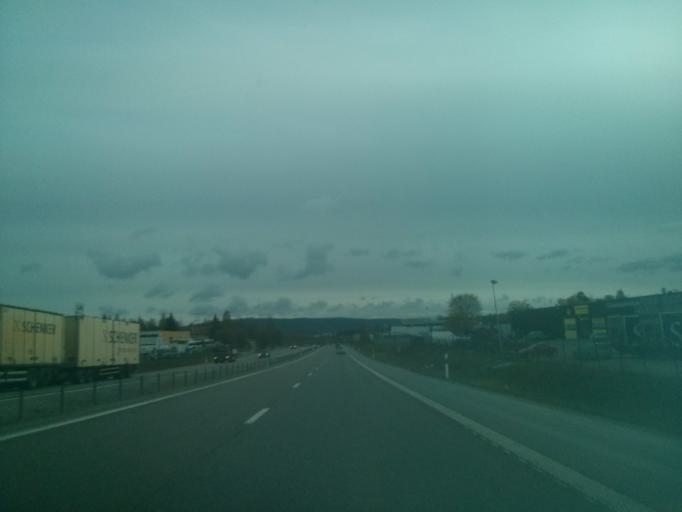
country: SE
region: Vaesternorrland
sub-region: Sundsvalls Kommun
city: Johannedal
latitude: 62.4182
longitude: 17.3456
